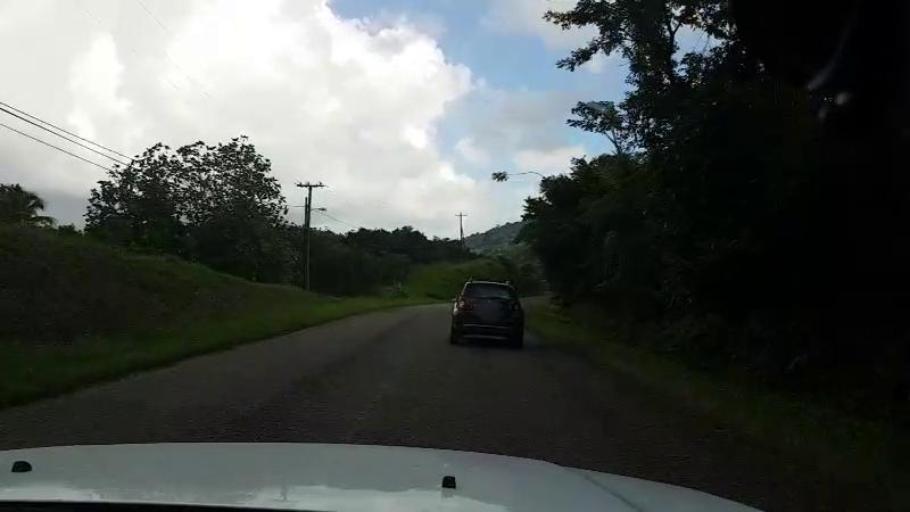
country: BZ
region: Stann Creek
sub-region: Dangriga
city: Dangriga
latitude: 17.0008
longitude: -88.4328
